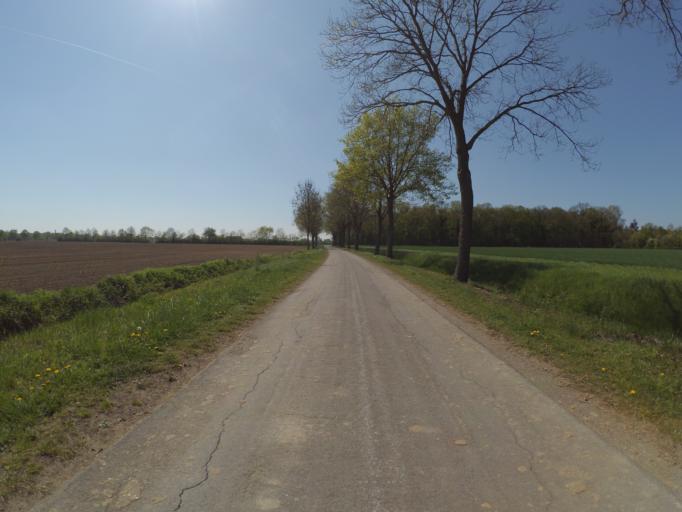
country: DE
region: North Rhine-Westphalia
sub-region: Regierungsbezirk Munster
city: Ascheberg
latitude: 51.7989
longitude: 7.6082
